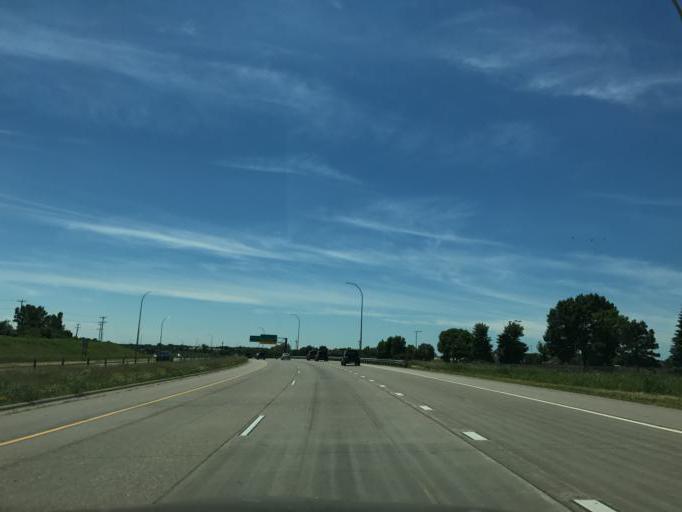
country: US
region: Minnesota
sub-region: Hennepin County
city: Osseo
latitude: 45.1005
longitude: -93.4017
